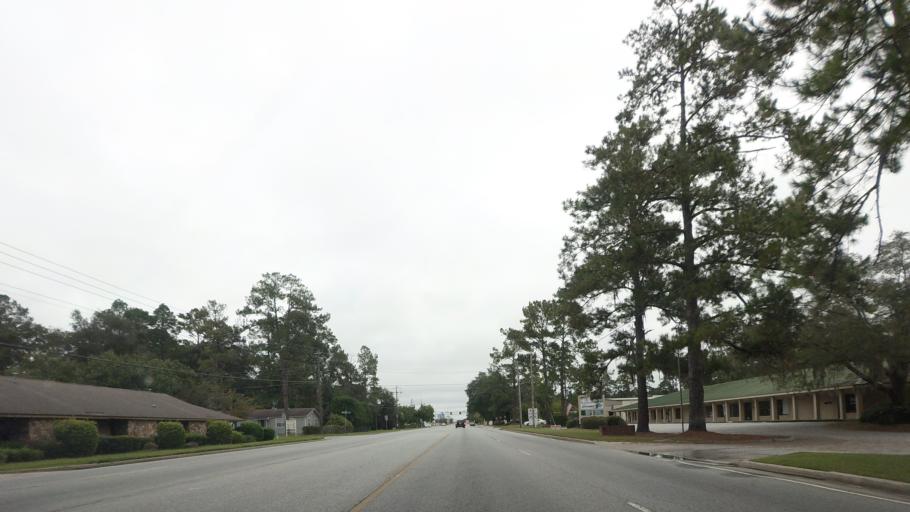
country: US
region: Georgia
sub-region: Lowndes County
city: Valdosta
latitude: 30.8702
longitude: -83.2783
